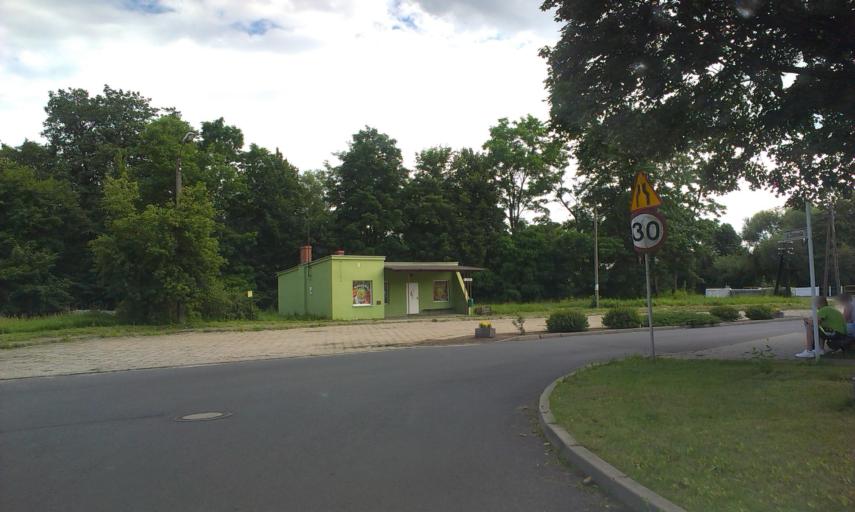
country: PL
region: Greater Poland Voivodeship
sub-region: Powiat zlotowski
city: Okonek
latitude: 53.5349
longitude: 16.9533
